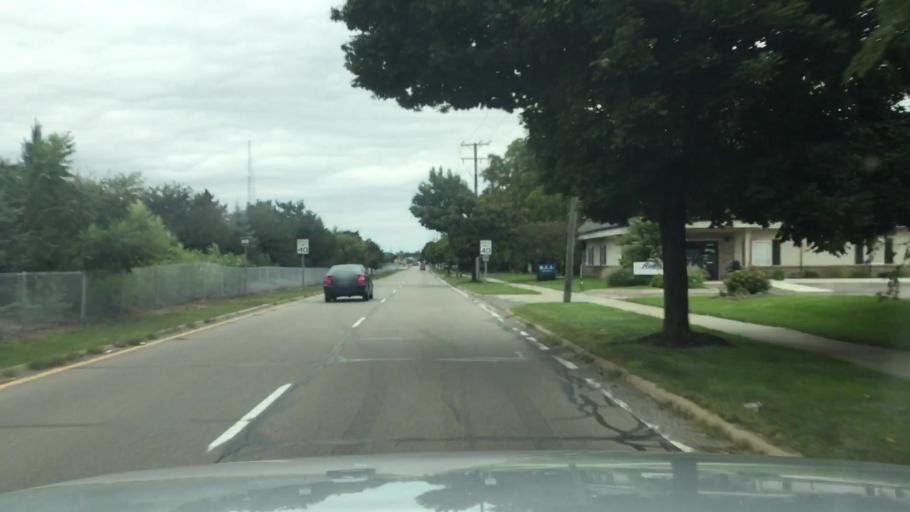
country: US
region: Michigan
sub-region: Macomb County
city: Roseville
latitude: 42.4945
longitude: -82.9604
